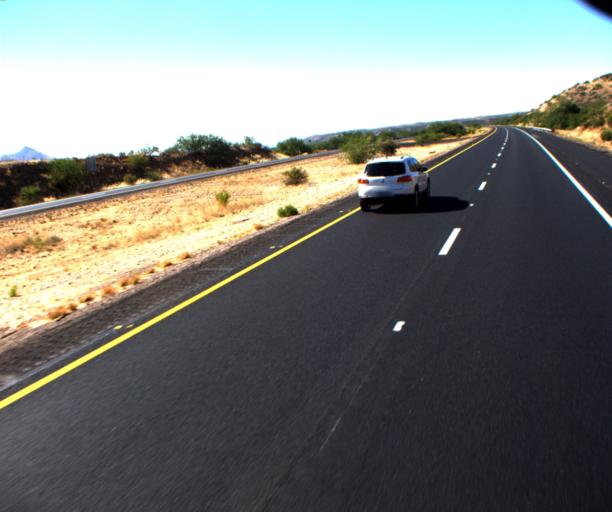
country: US
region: Arizona
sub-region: Santa Cruz County
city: Tubac
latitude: 31.5703
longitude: -111.0545
